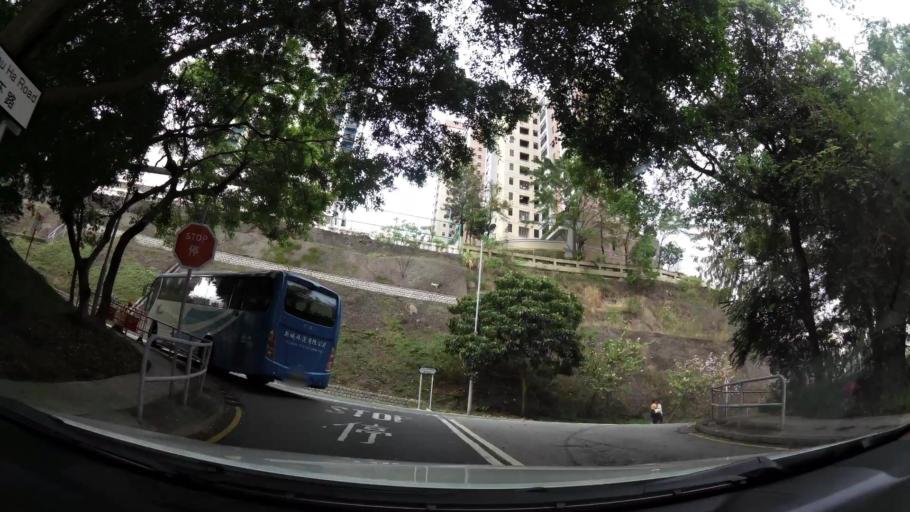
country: HK
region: Sha Tin
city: Sha Tin
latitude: 22.4008
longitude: 114.1967
